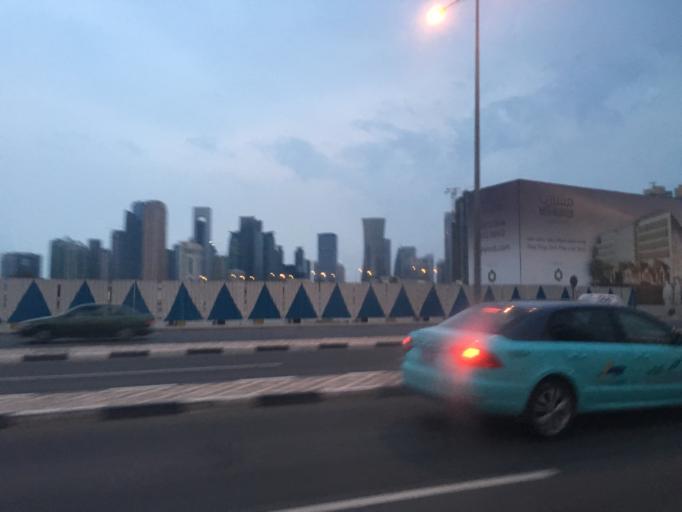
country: QA
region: Baladiyat ad Dawhah
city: Doha
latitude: 25.3210
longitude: 51.5115
